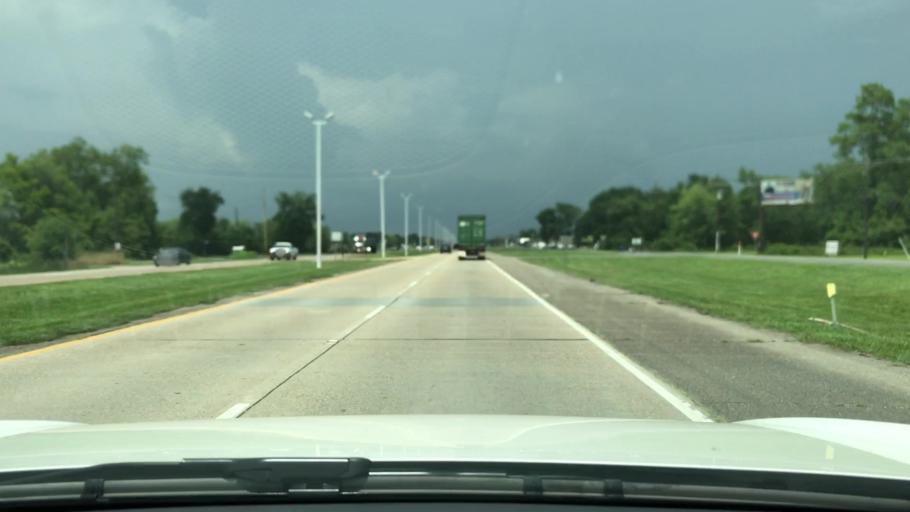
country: US
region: Louisiana
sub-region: West Baton Rouge Parish
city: Addis
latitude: 30.3680
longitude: -91.2585
